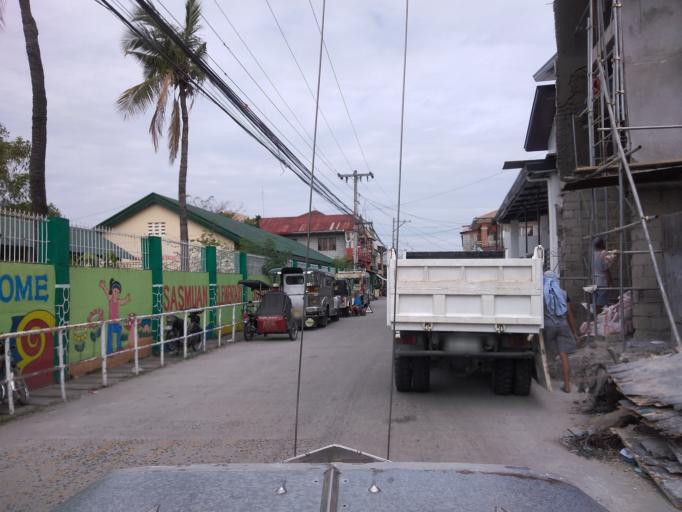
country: PH
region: Central Luzon
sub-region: Province of Pampanga
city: Sexmoan
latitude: 14.9376
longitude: 120.6218
